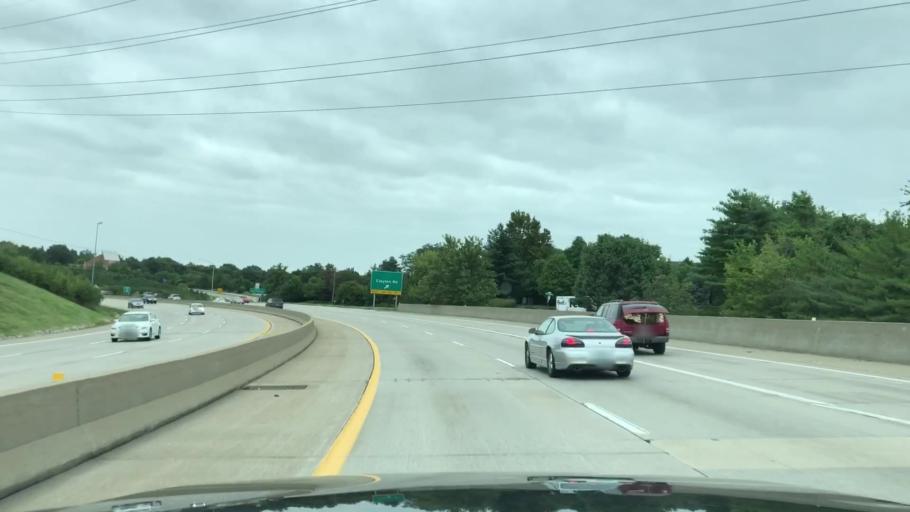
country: US
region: Missouri
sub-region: Saint Louis County
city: Manchester
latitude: 38.6192
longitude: -90.5105
